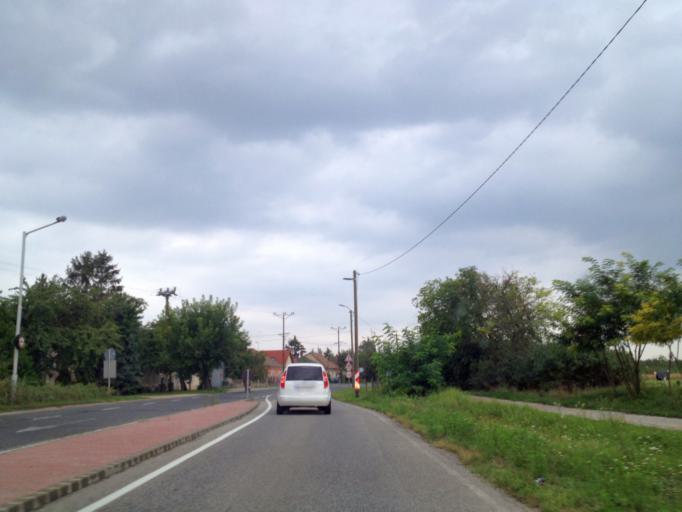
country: HU
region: Gyor-Moson-Sopron
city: Rajka
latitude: 47.9104
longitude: 17.1702
